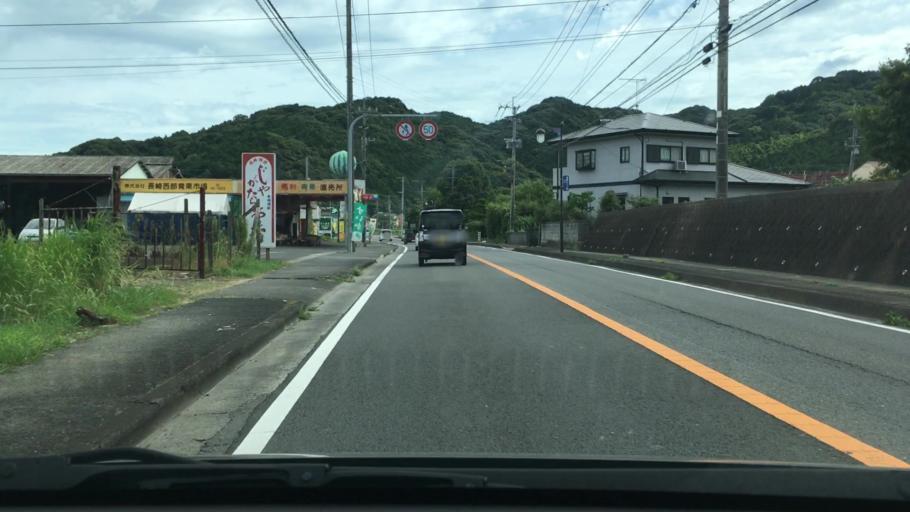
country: JP
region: Nagasaki
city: Togitsu
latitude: 32.8961
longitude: 129.7806
